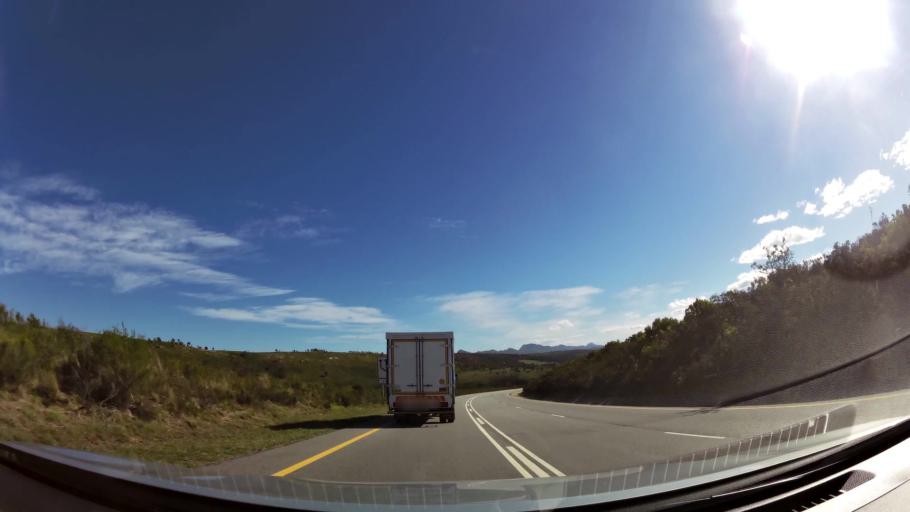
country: ZA
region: Eastern Cape
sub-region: Cacadu District Municipality
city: Kruisfontein
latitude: -34.0416
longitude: 24.5836
